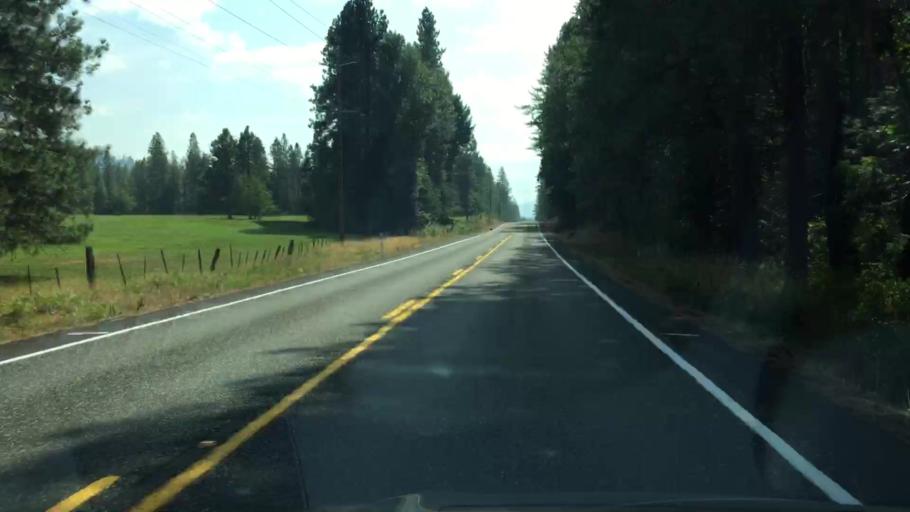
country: US
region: Washington
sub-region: Klickitat County
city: White Salmon
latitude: 45.9412
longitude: -121.4919
